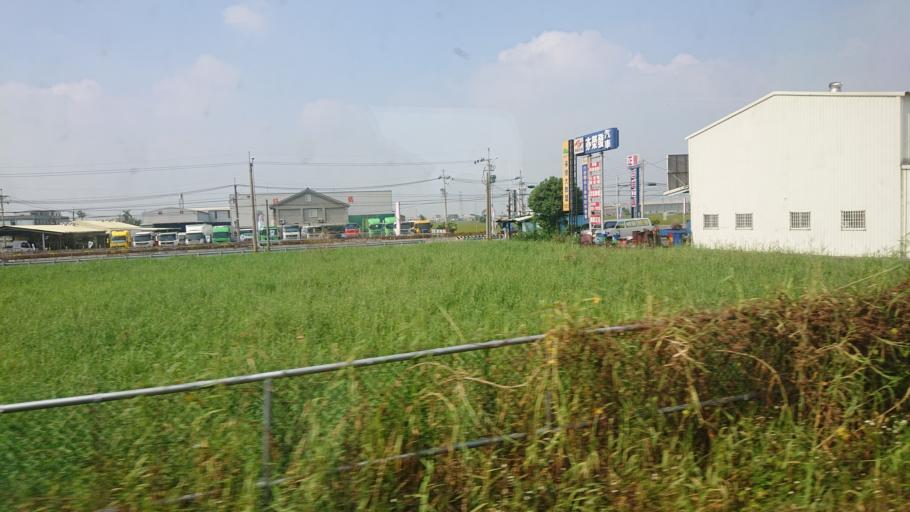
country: TW
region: Taiwan
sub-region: Yunlin
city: Douliu
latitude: 23.6535
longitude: 120.4732
